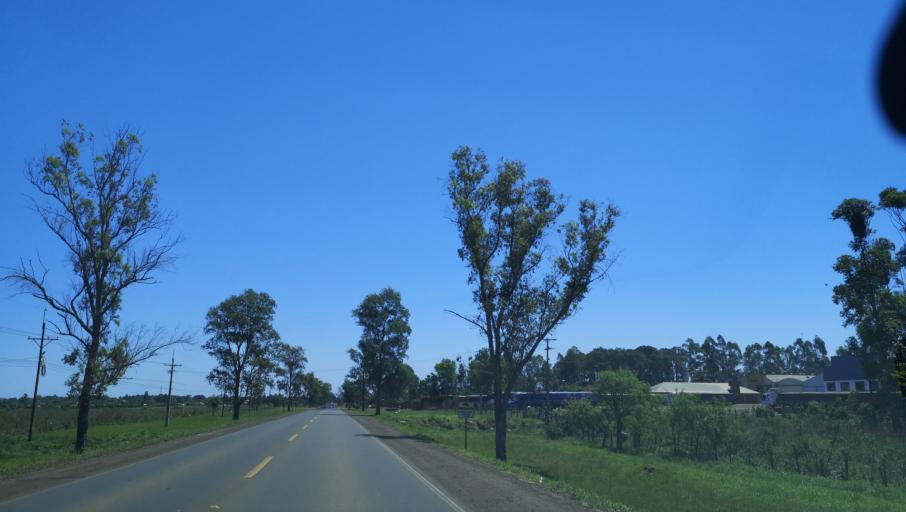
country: PY
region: Itapua
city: Carmen del Parana
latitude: -27.2208
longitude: -56.1284
